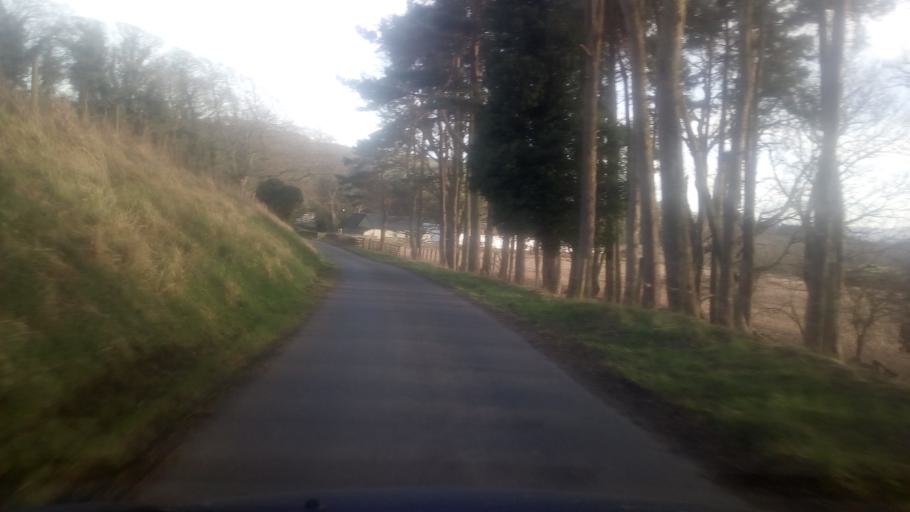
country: GB
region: Scotland
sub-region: The Scottish Borders
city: Jedburgh
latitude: 55.4563
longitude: -2.6355
